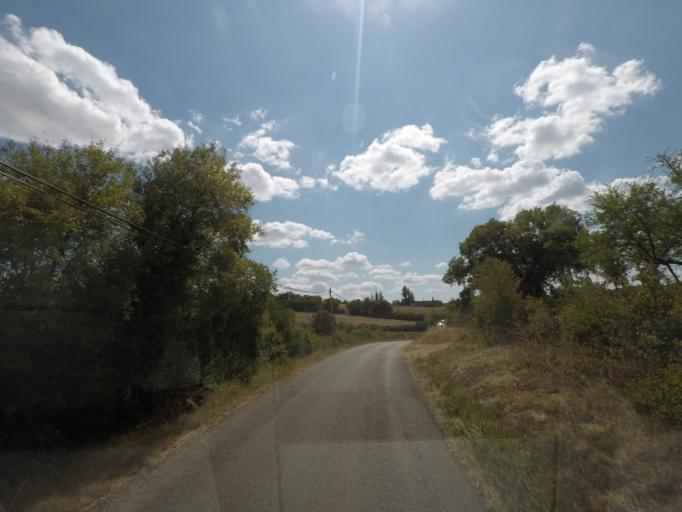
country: FR
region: Midi-Pyrenees
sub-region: Departement du Lot
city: Cajarc
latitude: 44.5512
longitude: 1.6722
